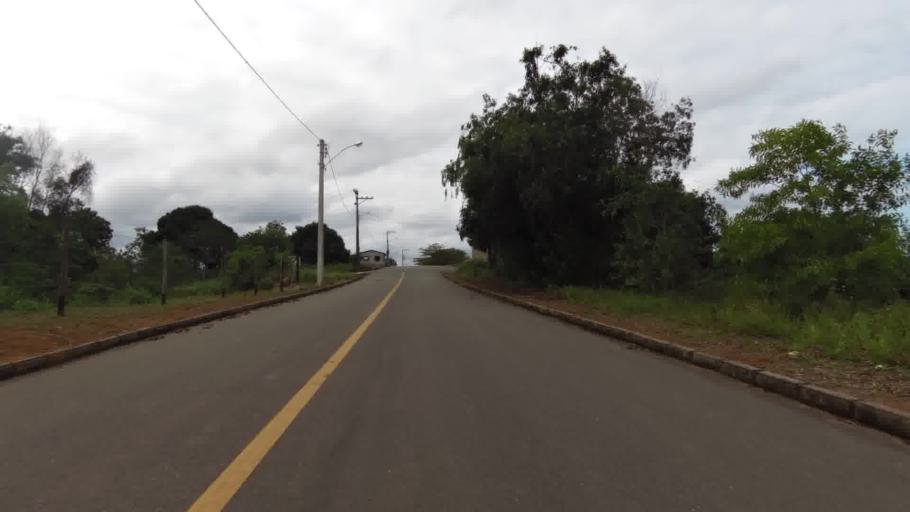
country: BR
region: Espirito Santo
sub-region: Piuma
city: Piuma
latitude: -20.8001
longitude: -40.6456
